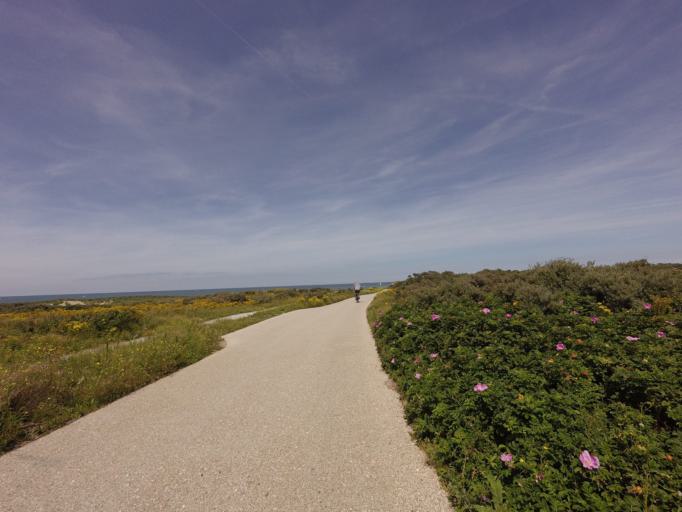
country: NL
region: South Holland
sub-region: Gemeente Den Haag
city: Scheveningen
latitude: 52.0868
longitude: 4.2470
